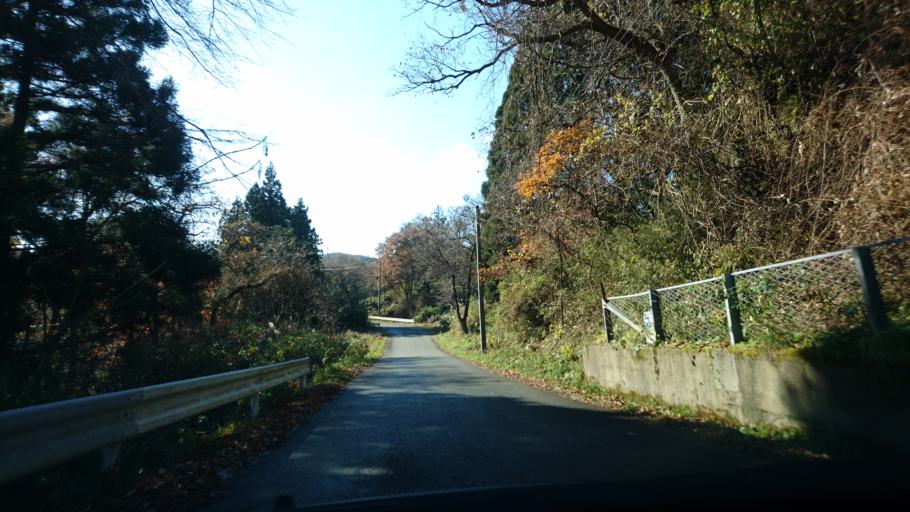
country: JP
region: Iwate
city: Ichinoseki
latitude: 38.9994
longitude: 141.0695
